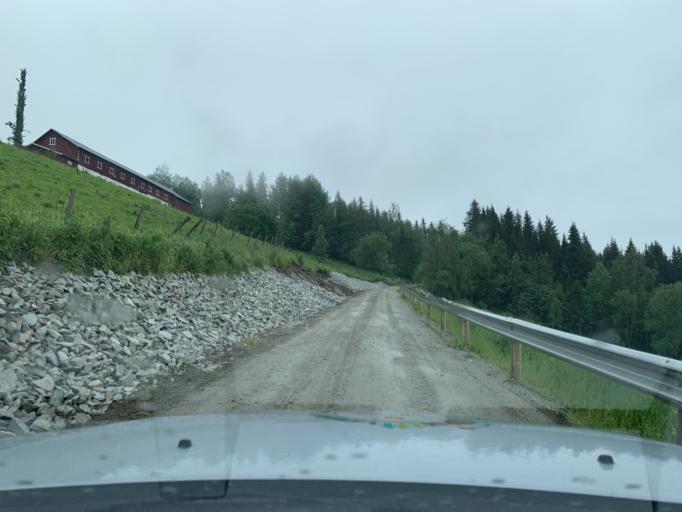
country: NO
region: Oppland
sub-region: Oyer
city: Tretten
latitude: 61.3871
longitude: 10.2822
